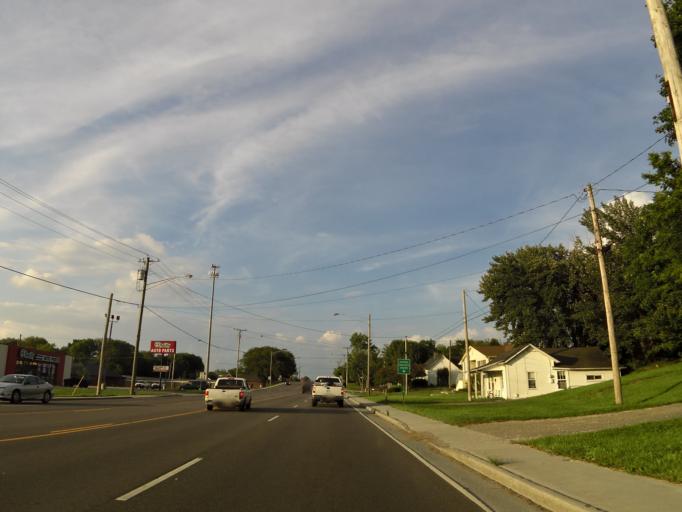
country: US
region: Tennessee
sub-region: Anderson County
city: Clinton
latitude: 36.1073
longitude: -84.1278
